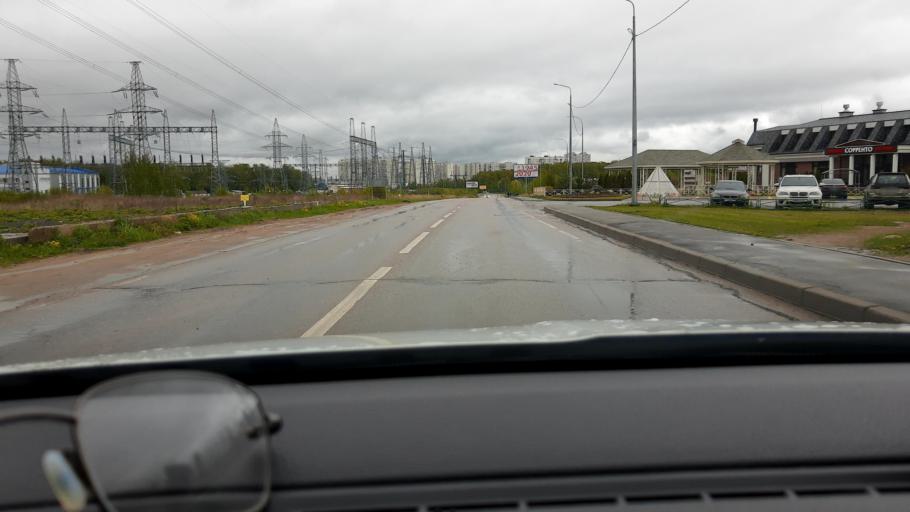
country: RU
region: Moskovskaya
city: Krasnogorsk
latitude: 55.8610
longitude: 37.3250
